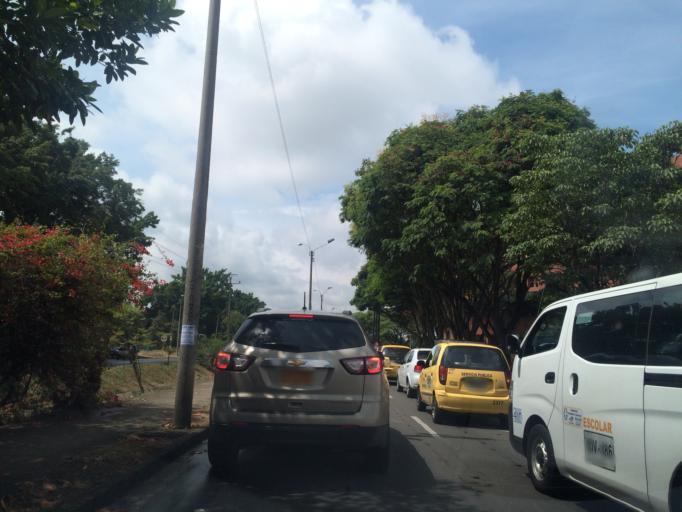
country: CO
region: Valle del Cauca
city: Cali
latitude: 3.3737
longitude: -76.5254
